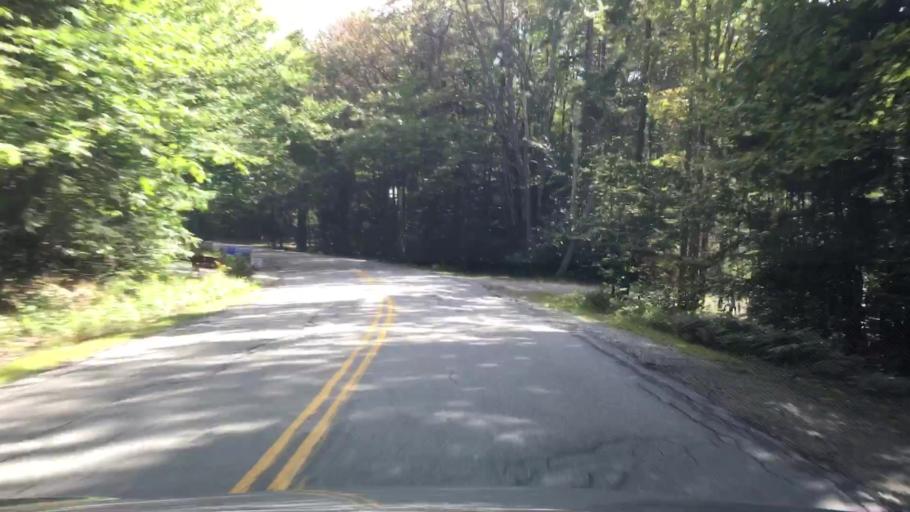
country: US
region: New Hampshire
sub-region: Carroll County
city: Tamworth
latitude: 44.0012
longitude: -71.3221
